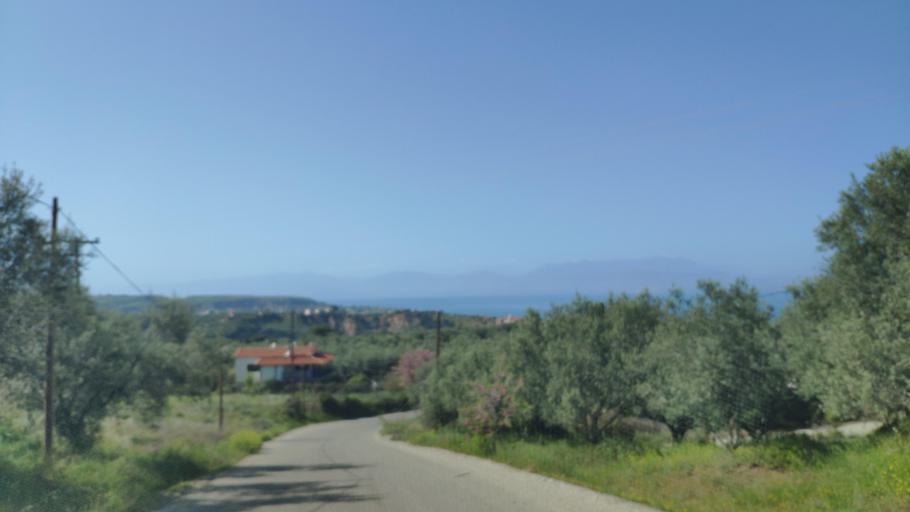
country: GR
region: West Greece
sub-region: Nomos Achaias
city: Aiyira
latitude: 38.1351
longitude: 22.3482
